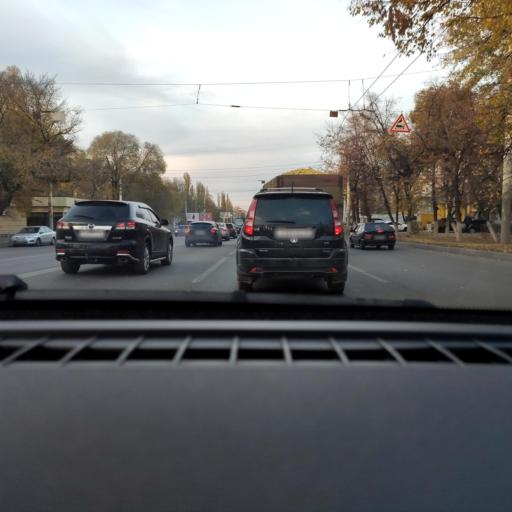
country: RU
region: Voronezj
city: Voronezh
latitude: 51.6294
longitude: 39.2305
